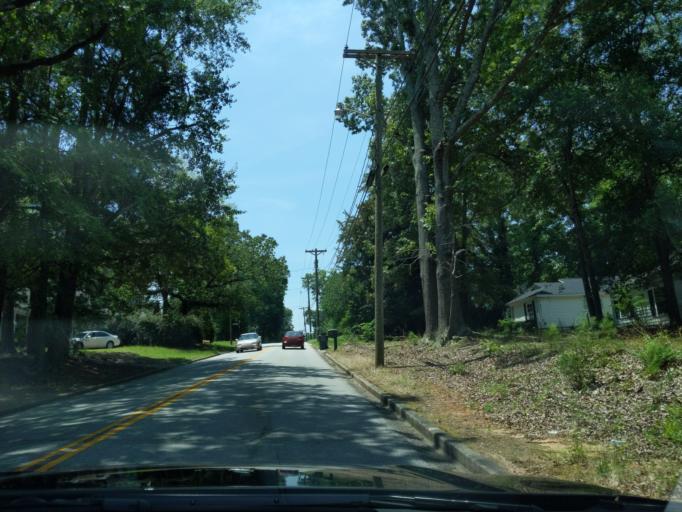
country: US
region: South Carolina
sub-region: Laurens County
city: Laurens
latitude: 34.4907
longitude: -82.0207
